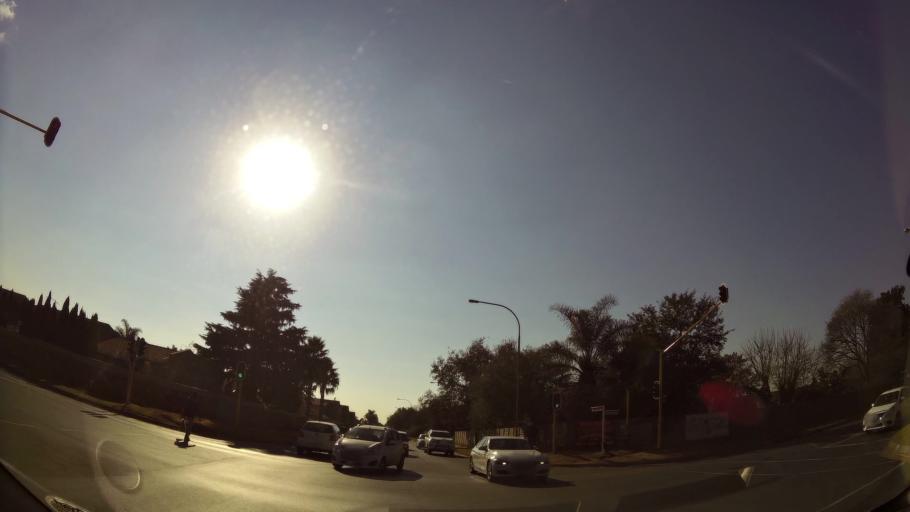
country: ZA
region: Gauteng
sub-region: Ekurhuleni Metropolitan Municipality
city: Benoni
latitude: -26.1475
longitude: 28.3139
